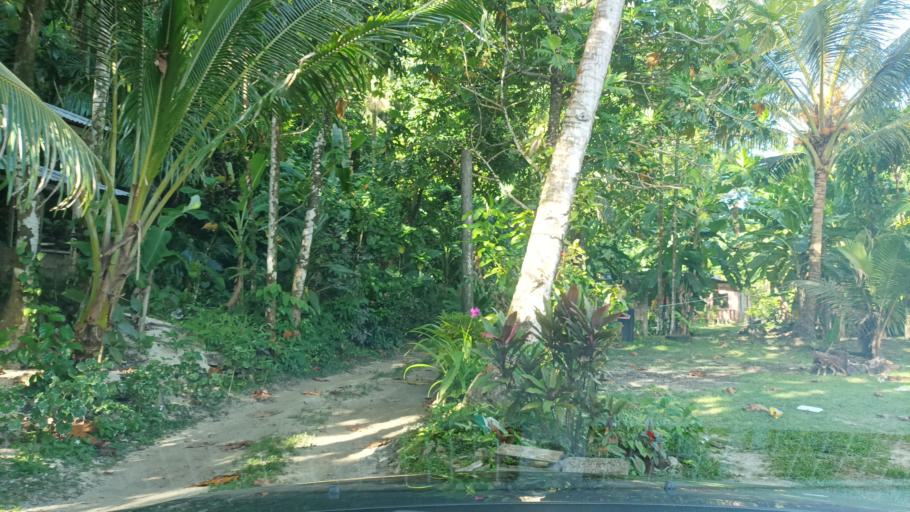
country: FM
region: Kosrae
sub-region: Lelu Municipality
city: Lelu
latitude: 5.3276
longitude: 163.0301
